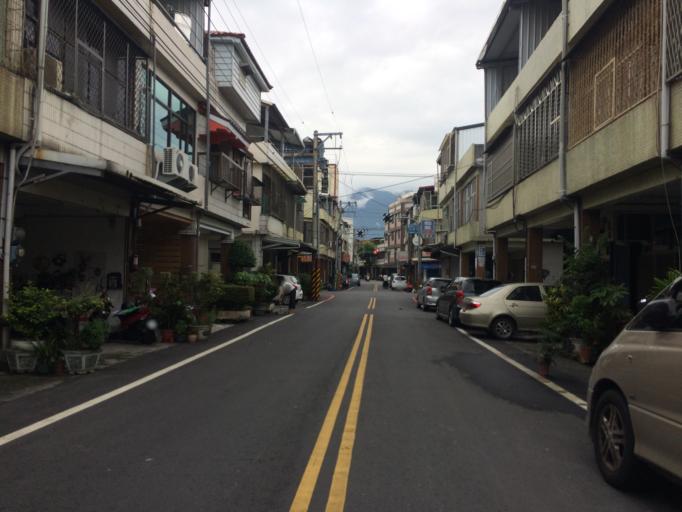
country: TW
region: Taiwan
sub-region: Hualien
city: Hualian
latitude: 23.9696
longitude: 121.6026
